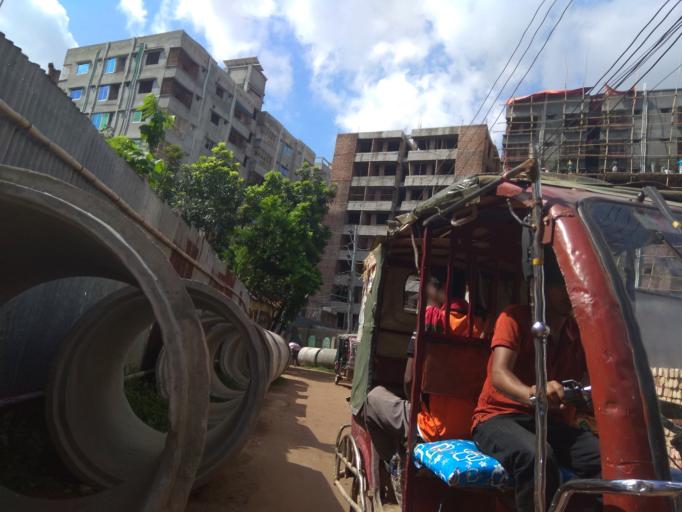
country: BD
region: Dhaka
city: Tungi
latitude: 23.8170
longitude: 90.3855
